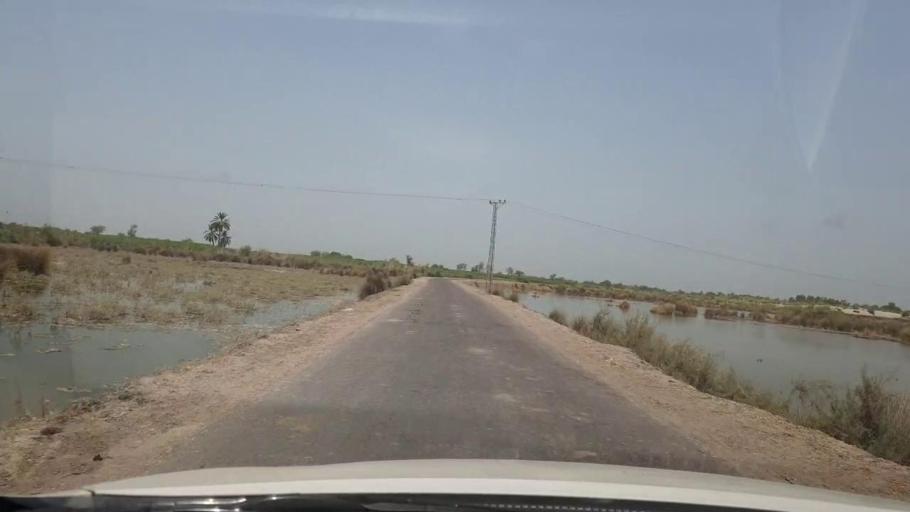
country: PK
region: Sindh
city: Bozdar
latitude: 27.2512
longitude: 68.6422
